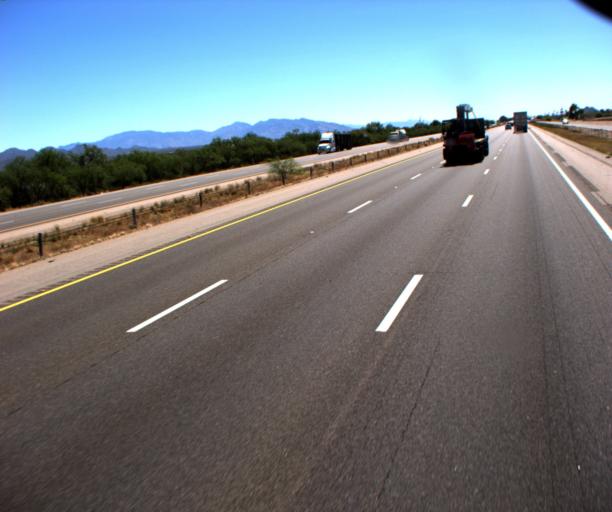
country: US
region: Arizona
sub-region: Pima County
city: Marana
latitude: 32.4710
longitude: -111.2292
